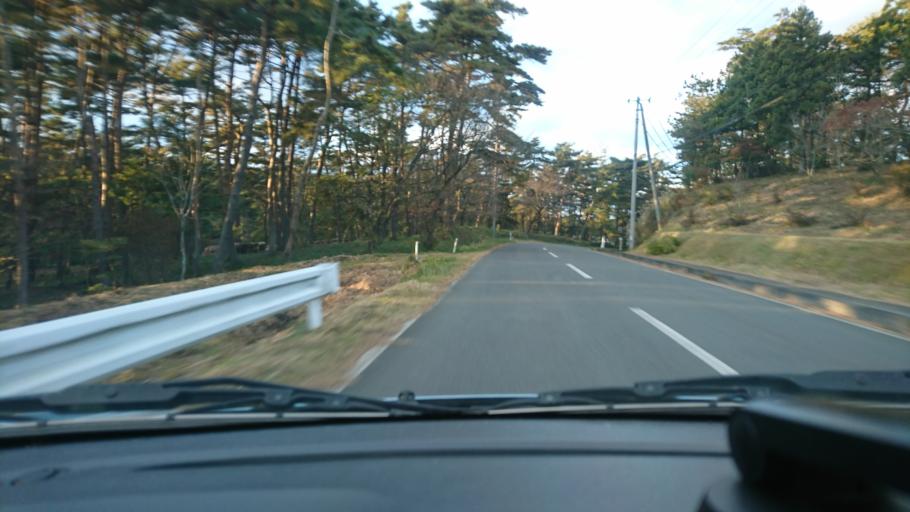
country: JP
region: Iwate
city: Ichinoseki
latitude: 38.8024
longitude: 141.1926
